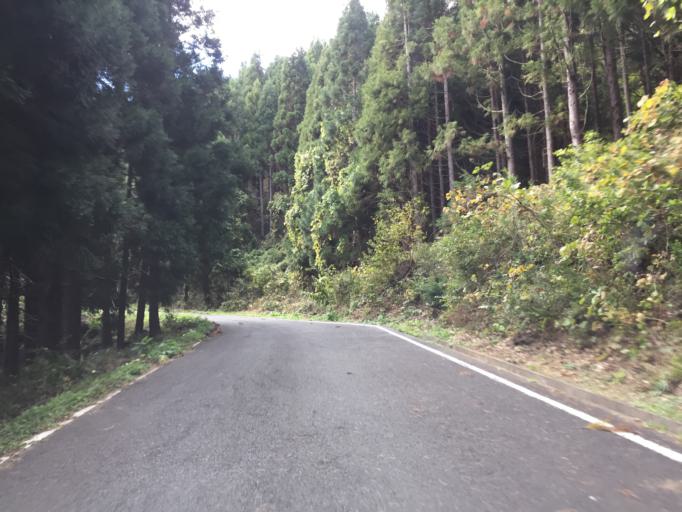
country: JP
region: Fukushima
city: Nihommatsu
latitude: 37.6764
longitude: 140.3863
